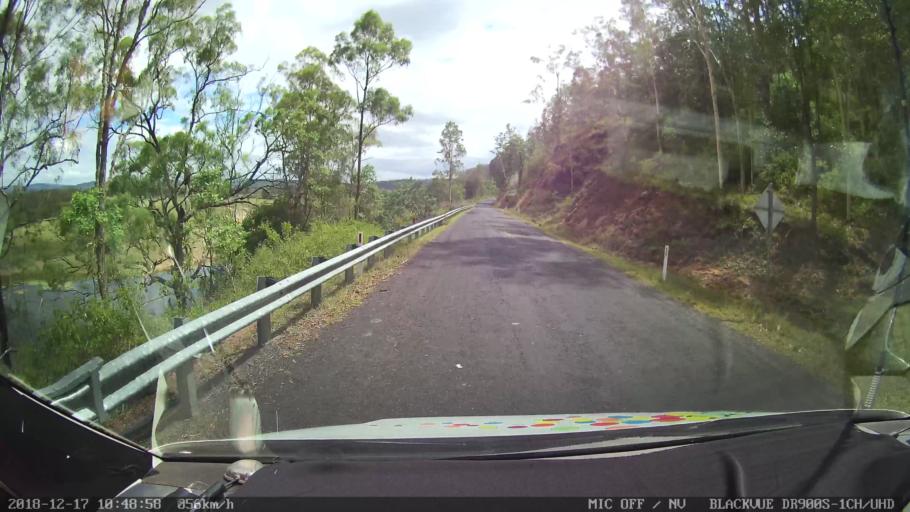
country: AU
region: New South Wales
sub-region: Clarence Valley
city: Gordon
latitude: -28.8693
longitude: 152.5717
